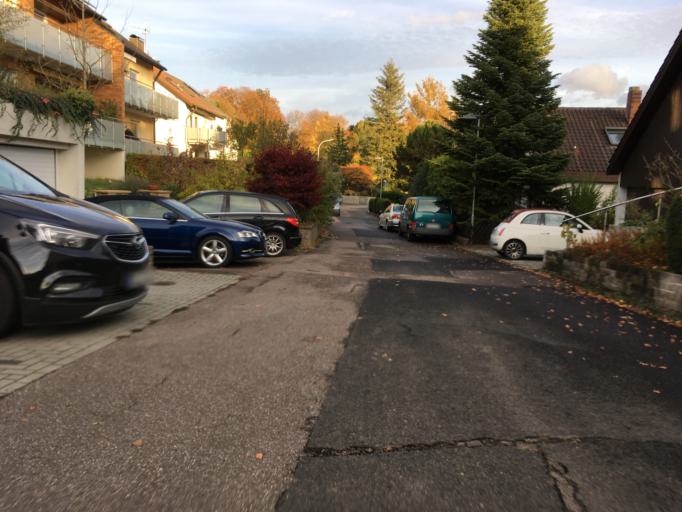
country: DE
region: Baden-Wuerttemberg
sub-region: Regierungsbezirk Stuttgart
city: Flein
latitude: 49.1169
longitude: 9.1998
